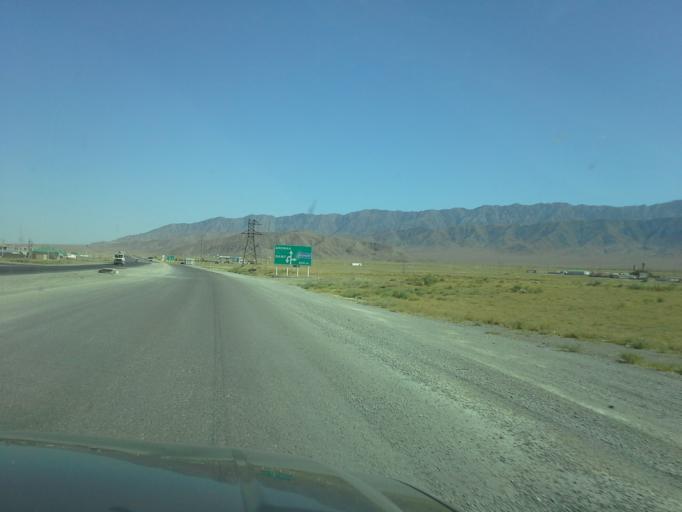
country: TM
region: Ahal
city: Baharly
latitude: 38.5438
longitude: 57.1484
